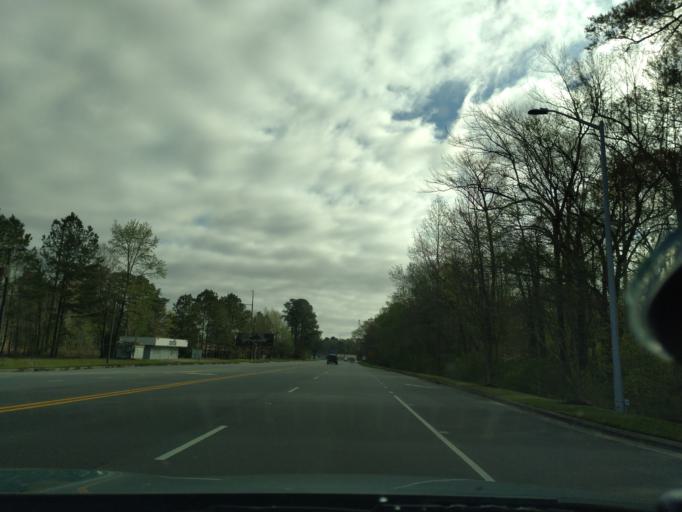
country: US
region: North Carolina
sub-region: Washington County
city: Plymouth
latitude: 35.8659
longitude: -76.7251
